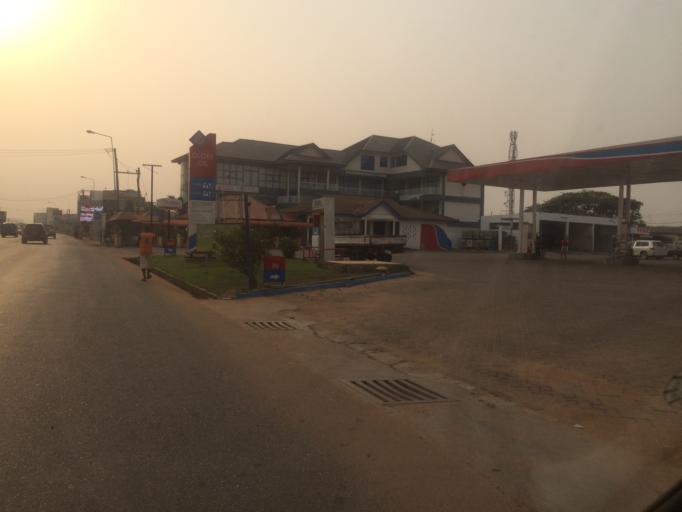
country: GH
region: Greater Accra
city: Nungua
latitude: 5.6365
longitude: -0.1032
